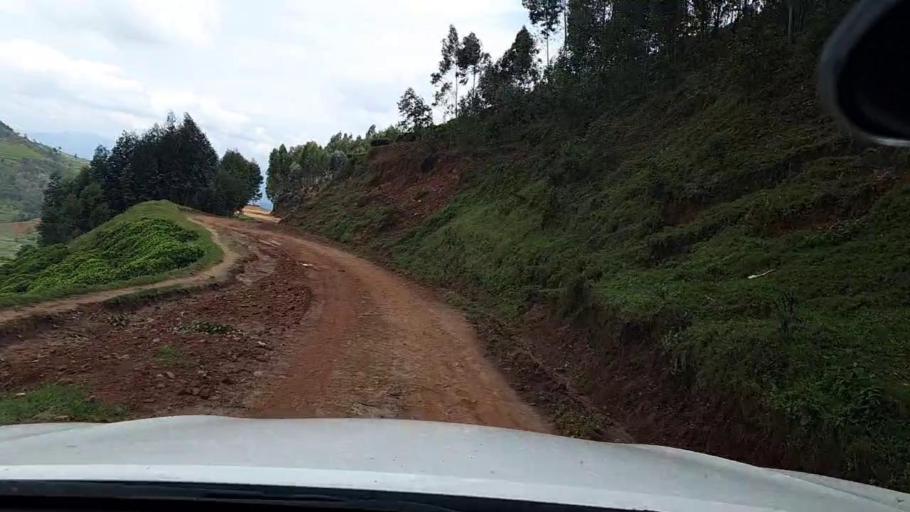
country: RW
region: Western Province
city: Kibuye
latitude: -2.1663
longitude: 29.3996
